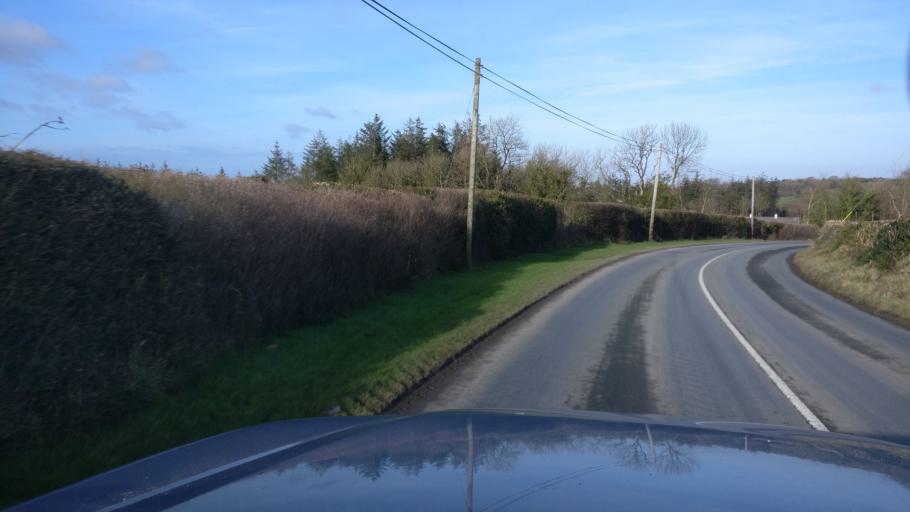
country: IE
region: Leinster
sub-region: Laois
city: Stradbally
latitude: 52.9332
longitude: -7.1981
